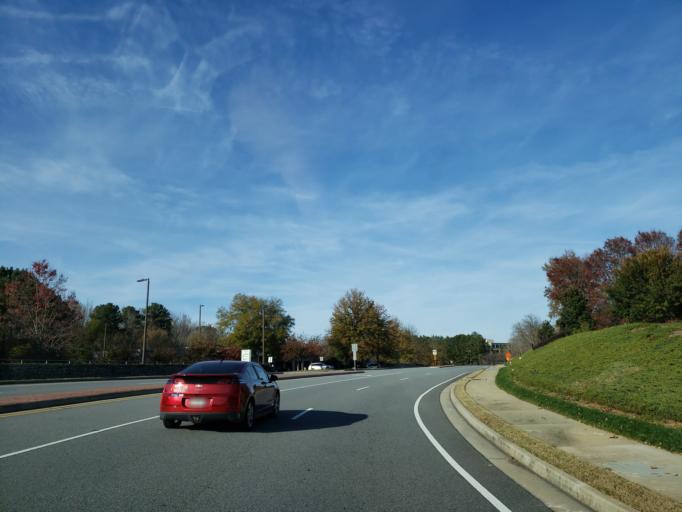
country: US
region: Georgia
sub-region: Cobb County
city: Kennesaw
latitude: 34.0255
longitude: -84.5822
